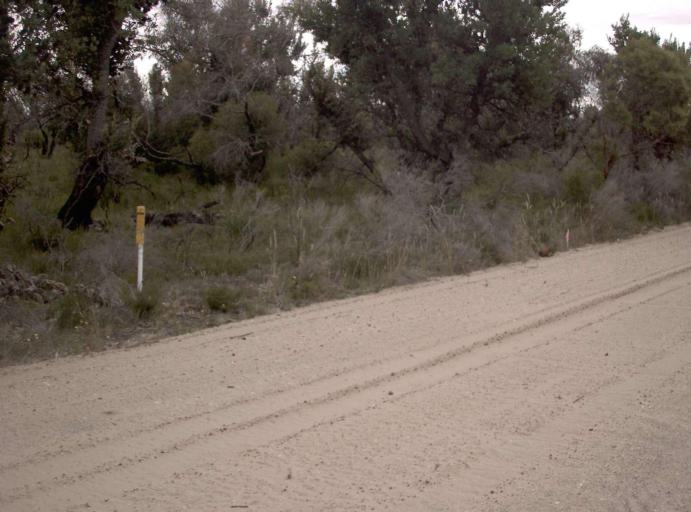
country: AU
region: Victoria
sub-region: East Gippsland
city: Bairnsdale
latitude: -38.1140
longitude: 147.4649
